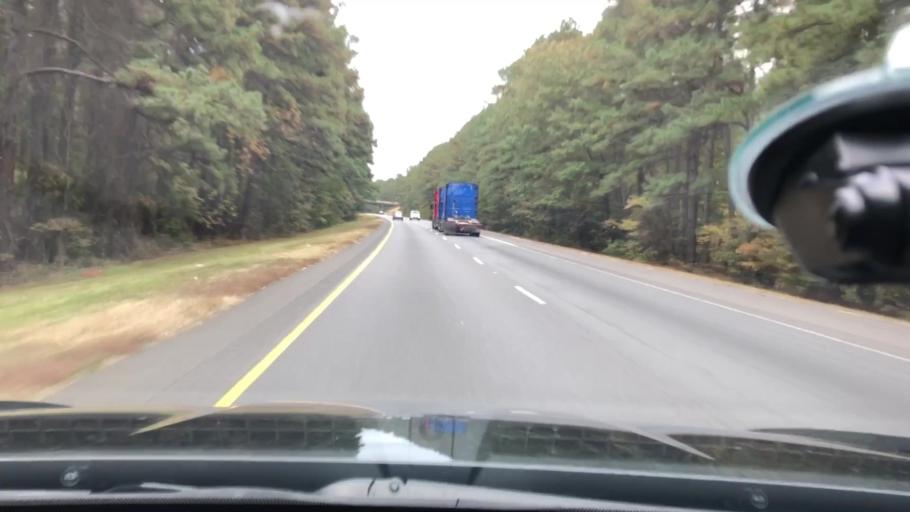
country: US
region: Arkansas
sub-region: Hot Spring County
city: Malvern
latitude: 34.2843
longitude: -92.9571
